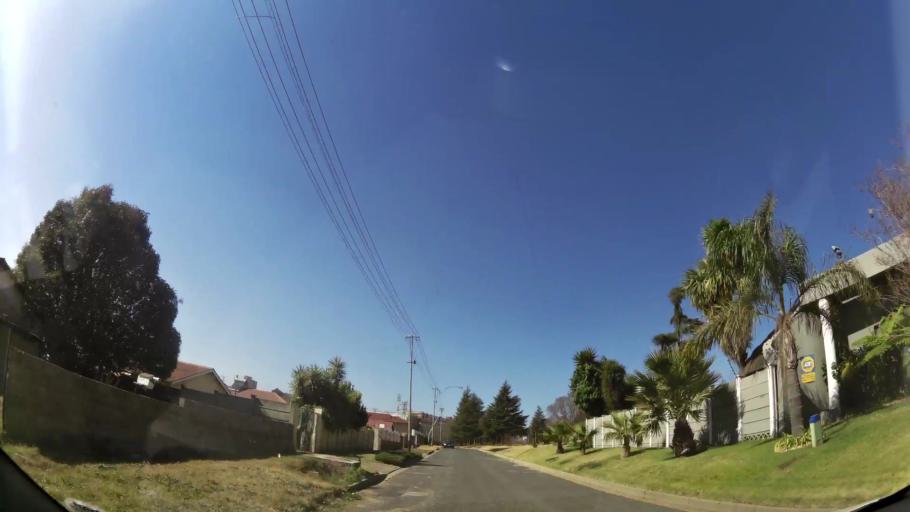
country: ZA
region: Gauteng
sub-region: City of Johannesburg Metropolitan Municipality
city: Johannesburg
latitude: -26.1921
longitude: 27.9616
